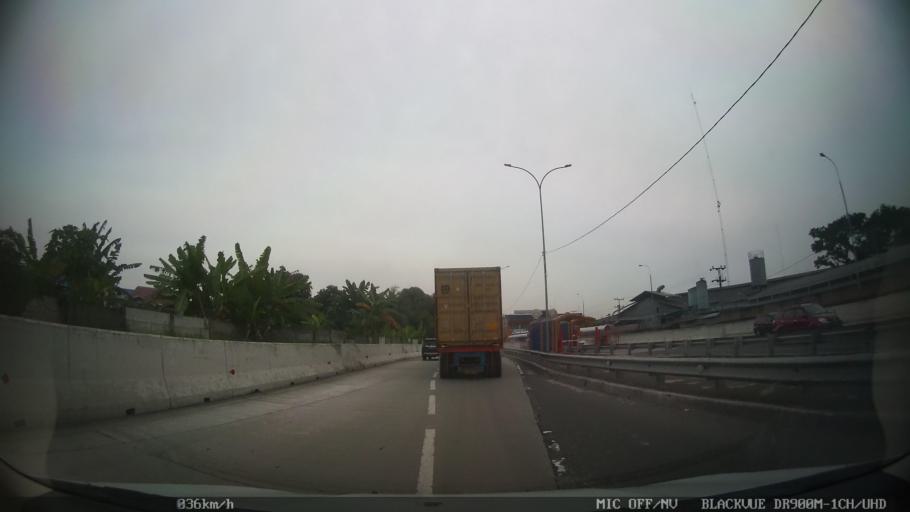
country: ID
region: North Sumatra
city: Deli Tua
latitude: 3.5398
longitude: 98.7233
